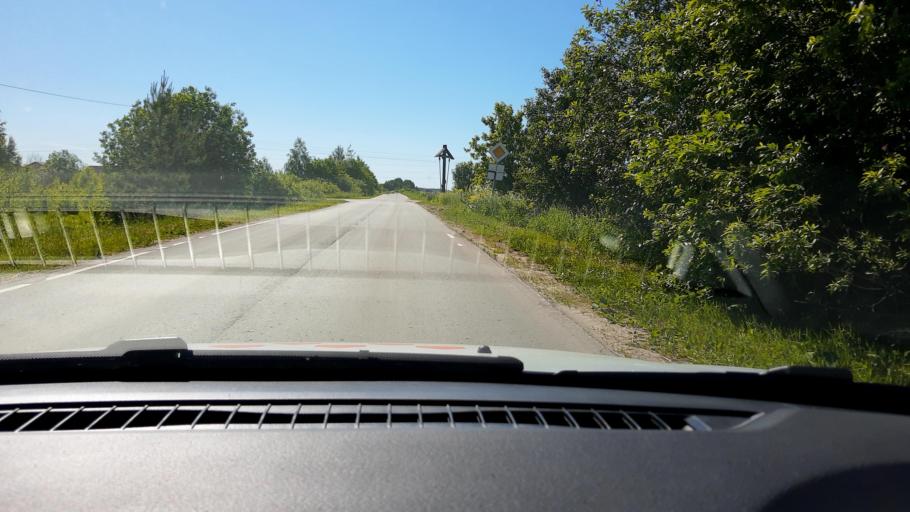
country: RU
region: Nizjnij Novgorod
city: Bor
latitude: 56.3954
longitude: 44.0794
